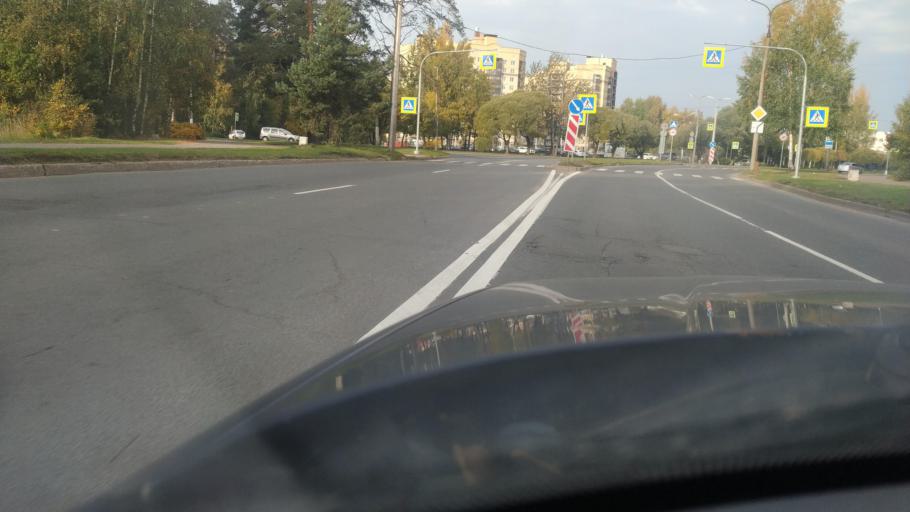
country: RU
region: Leningrad
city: Sosnovyy Bor
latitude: 59.8999
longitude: 29.1027
